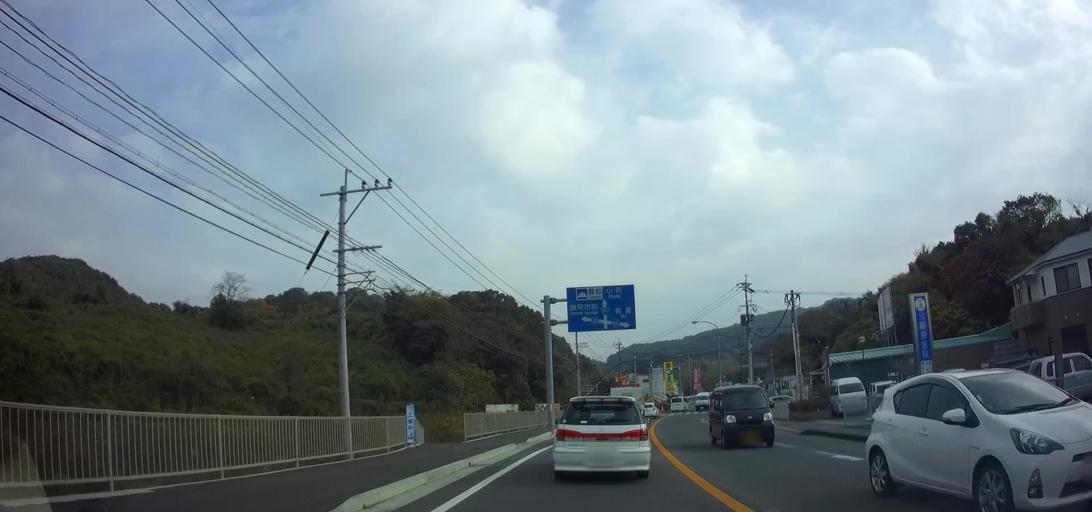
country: JP
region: Nagasaki
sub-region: Isahaya-shi
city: Isahaya
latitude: 32.7990
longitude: 130.0839
